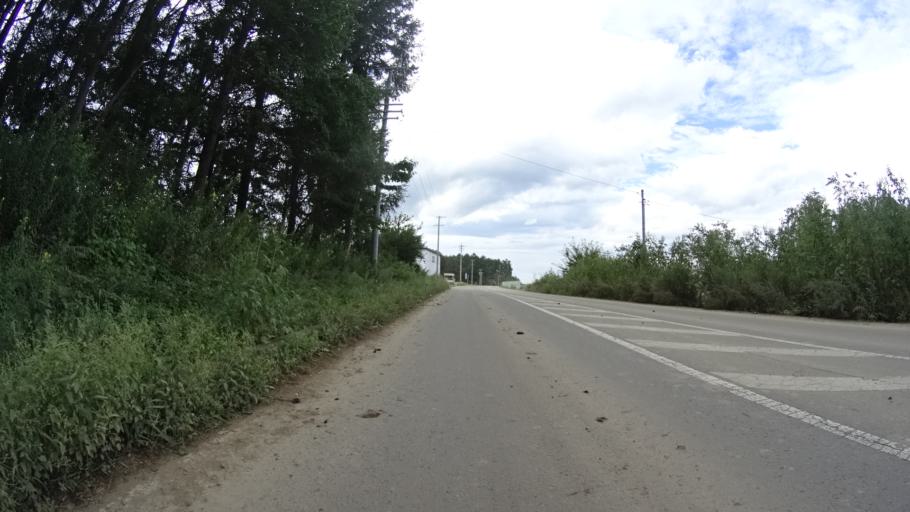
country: JP
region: Nagano
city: Saku
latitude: 35.9670
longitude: 138.5164
